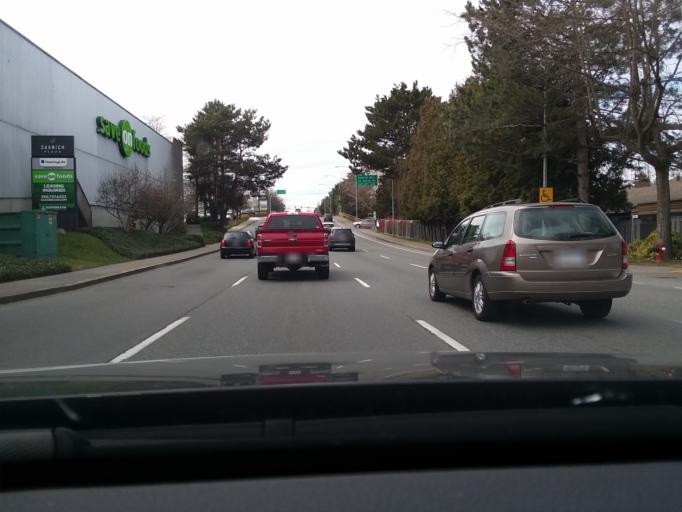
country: CA
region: British Columbia
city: Victoria
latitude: 48.4569
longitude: -123.3723
